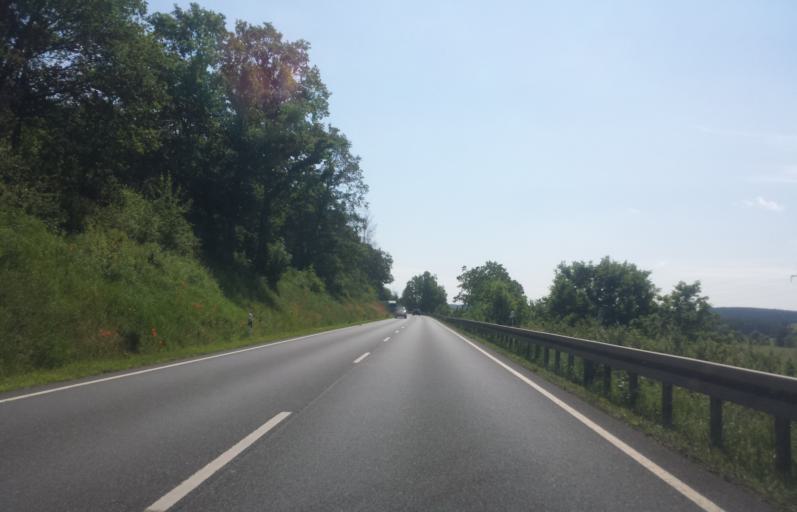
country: DE
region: Bavaria
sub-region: Upper Franconia
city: Altenkunstadt
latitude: 50.1292
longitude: 11.2643
